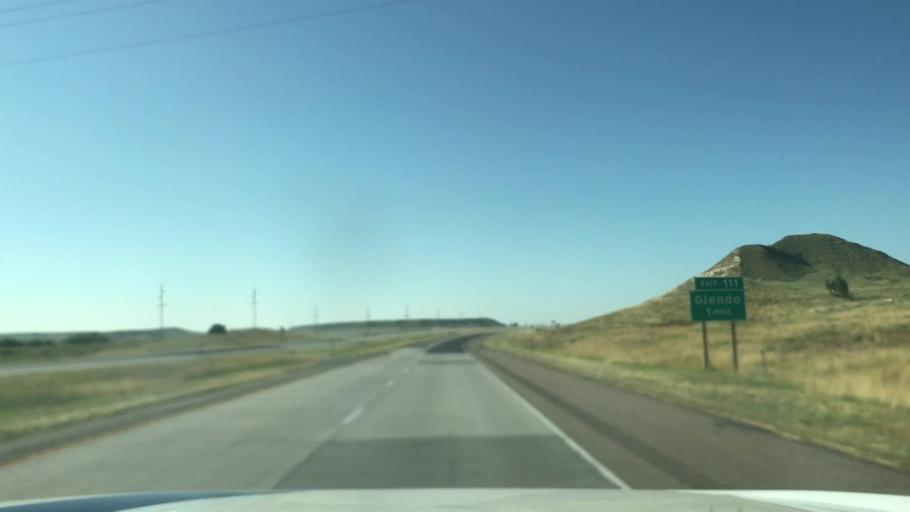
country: US
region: Wyoming
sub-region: Platte County
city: Guernsey
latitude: 42.5249
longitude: -105.0272
